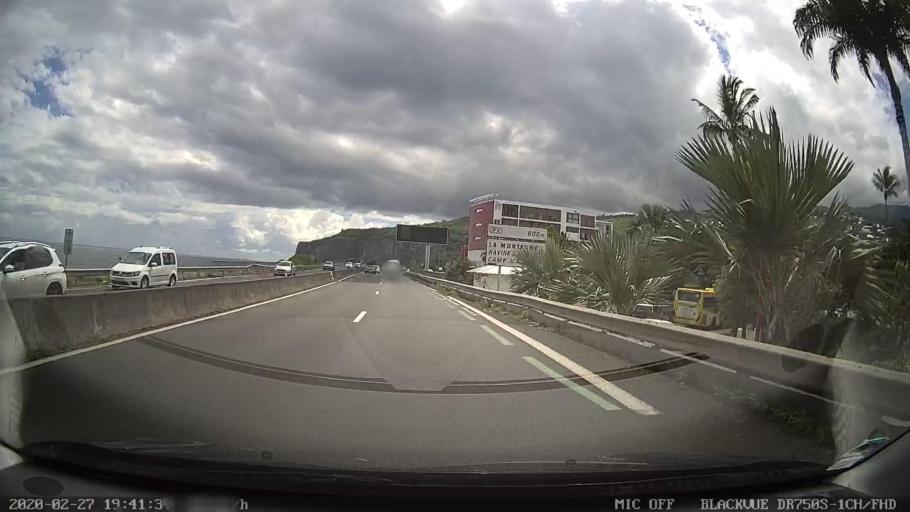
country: RE
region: Reunion
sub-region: Reunion
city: La Possession
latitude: -20.9246
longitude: 55.3365
